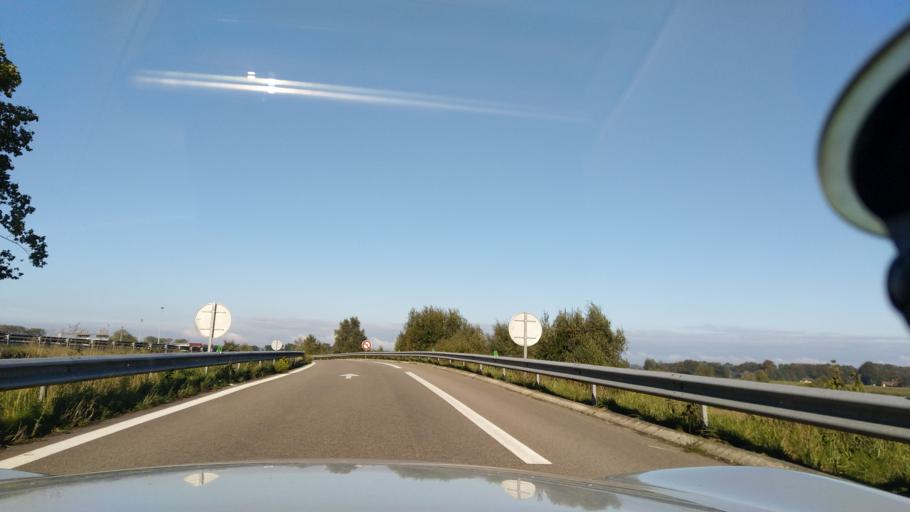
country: FR
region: Haute-Normandie
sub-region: Departement de la Seine-Maritime
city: Valliquerville
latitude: 49.6314
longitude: 0.6459
